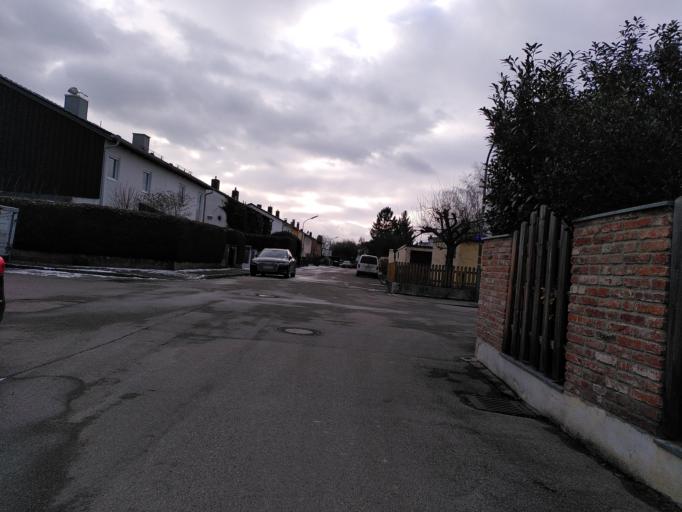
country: DE
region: Bavaria
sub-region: Upper Bavaria
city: Olching
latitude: 48.2007
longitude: 11.3299
